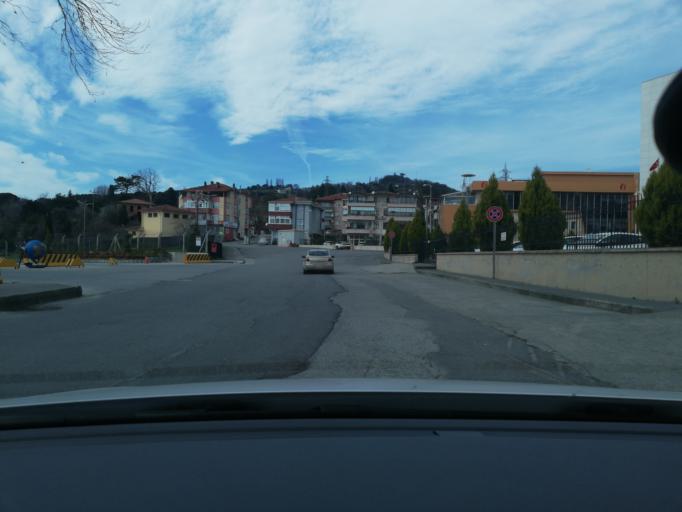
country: TR
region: Zonguldak
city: Eregli
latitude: 41.2907
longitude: 31.4073
